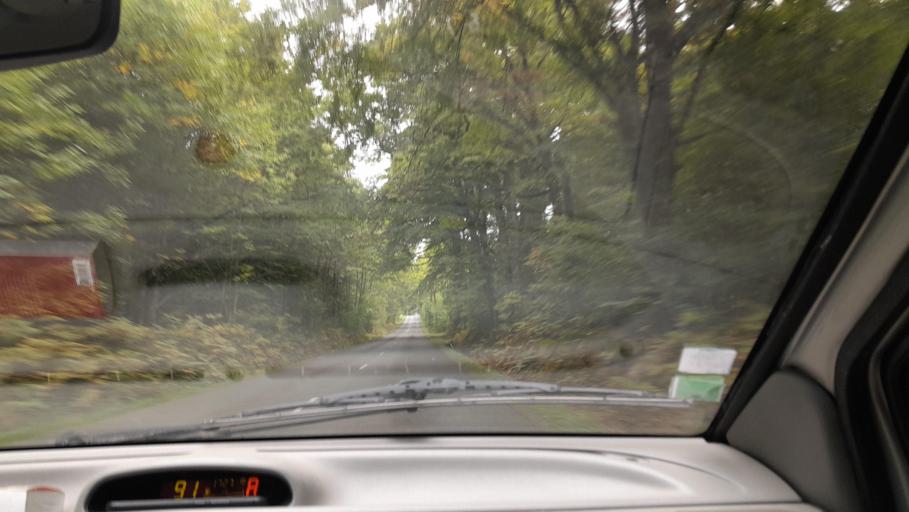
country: FR
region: Pays de la Loire
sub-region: Departement de Maine-et-Loire
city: Pouance
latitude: 47.7058
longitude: -1.1792
